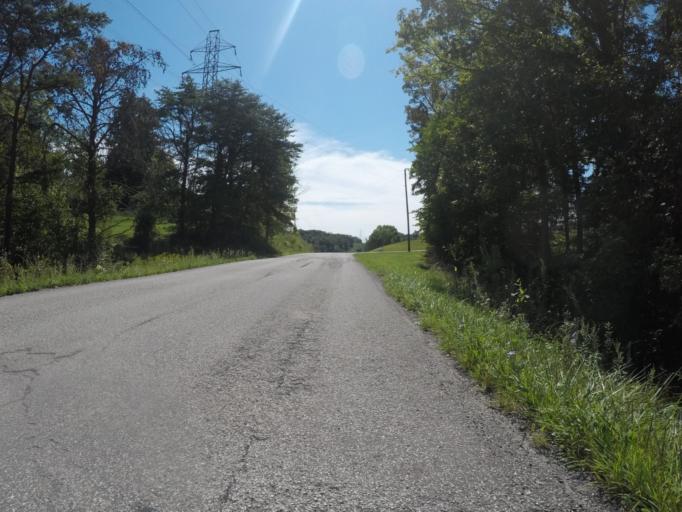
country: US
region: Kentucky
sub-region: Boyd County
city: Catlettsburg
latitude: 38.4048
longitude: -82.6514
